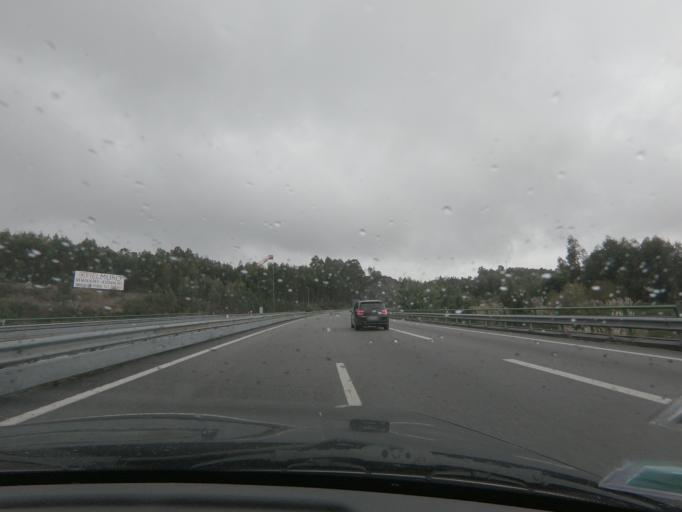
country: PT
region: Porto
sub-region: Valongo
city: Valongo
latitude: 41.1993
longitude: -8.5160
